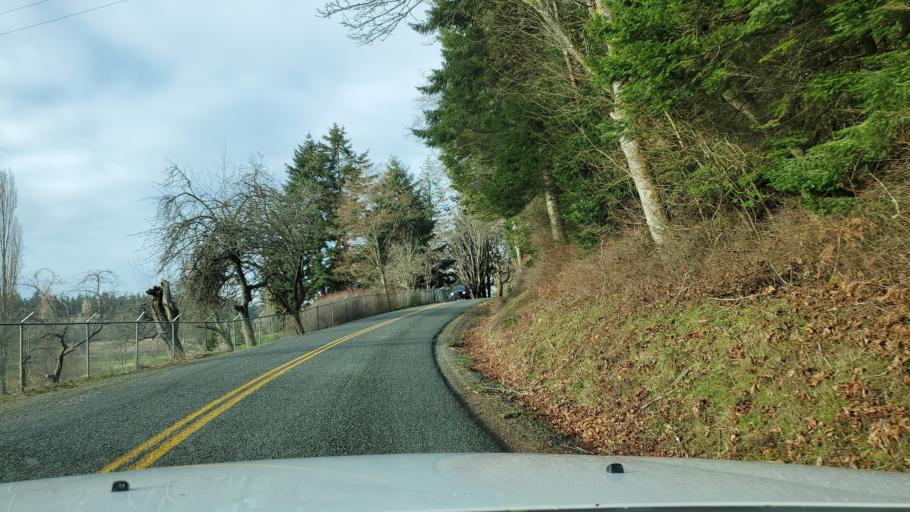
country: US
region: Washington
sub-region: Skagit County
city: Anacortes
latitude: 48.4532
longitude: -122.5750
